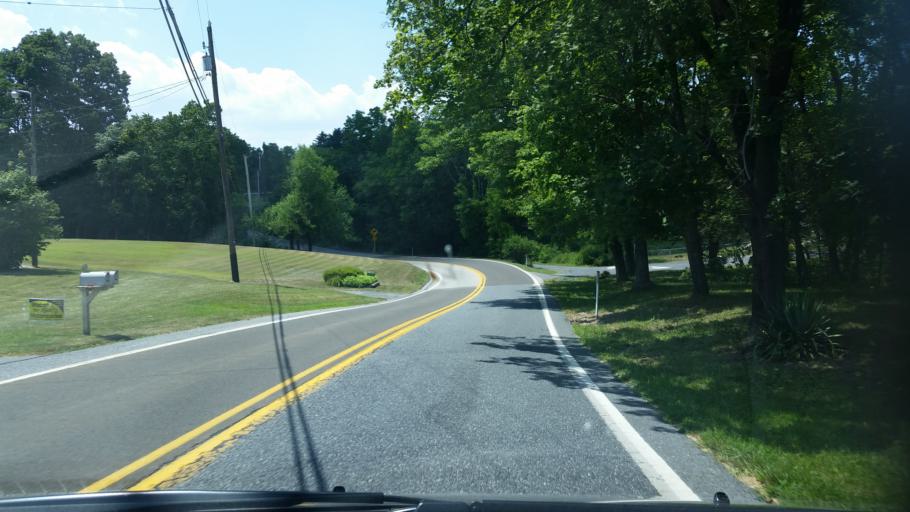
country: US
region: Pennsylvania
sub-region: Dauphin County
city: Hummelstown
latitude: 40.2872
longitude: -76.7190
